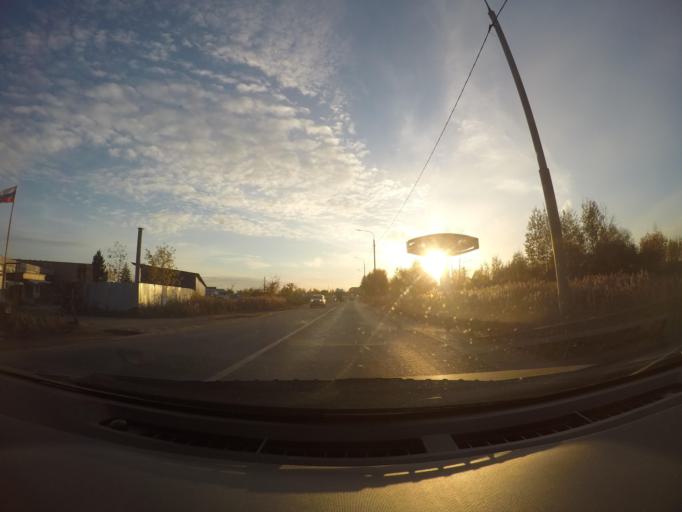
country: RU
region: Moskovskaya
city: Rzhavki
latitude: 55.9821
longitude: 37.2677
